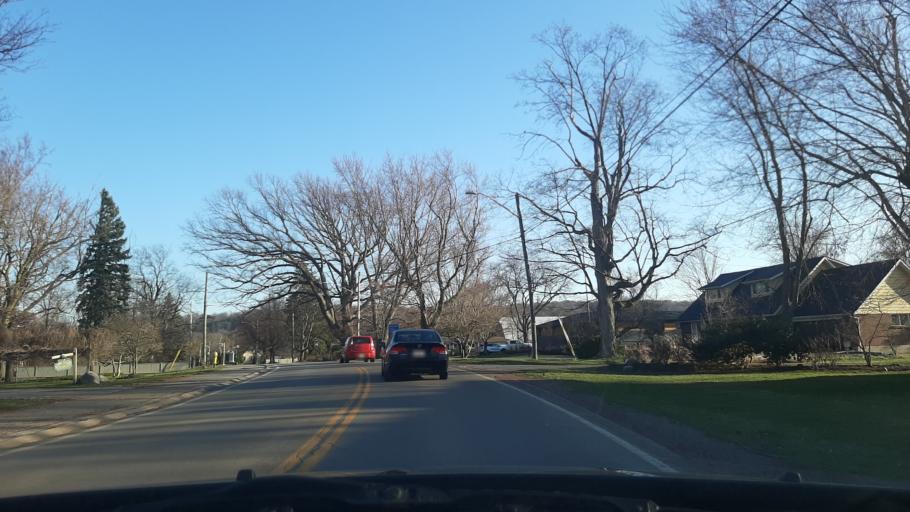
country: US
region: New York
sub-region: Niagara County
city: Lewiston
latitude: 43.1723
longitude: -79.0587
